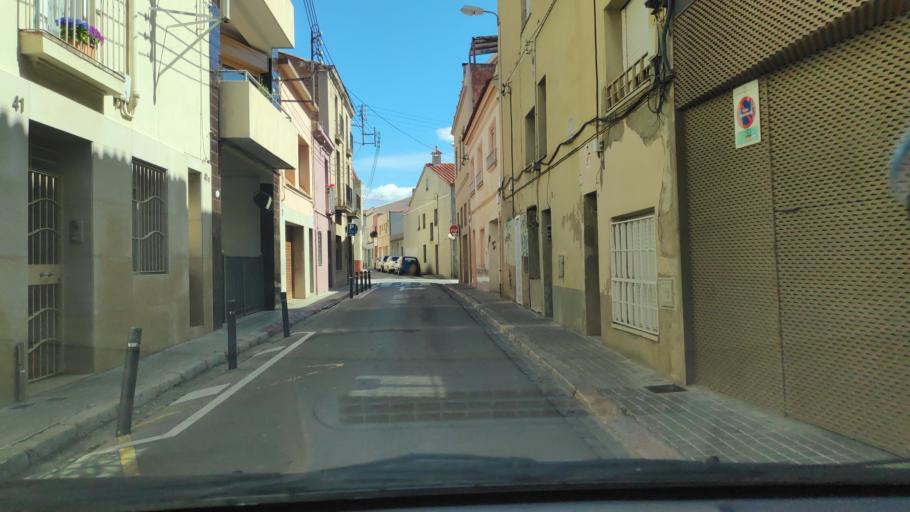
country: ES
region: Catalonia
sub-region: Provincia de Barcelona
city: Sabadell
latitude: 41.5516
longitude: 2.1095
